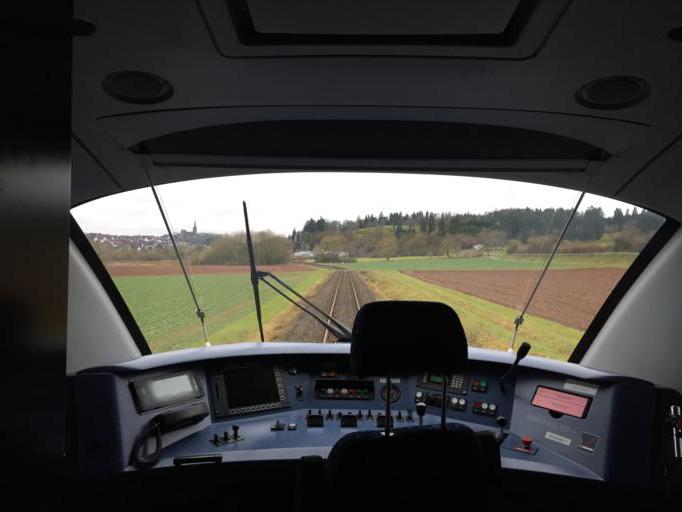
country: DE
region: Hesse
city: Frankenberg
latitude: 51.0742
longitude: 8.8077
